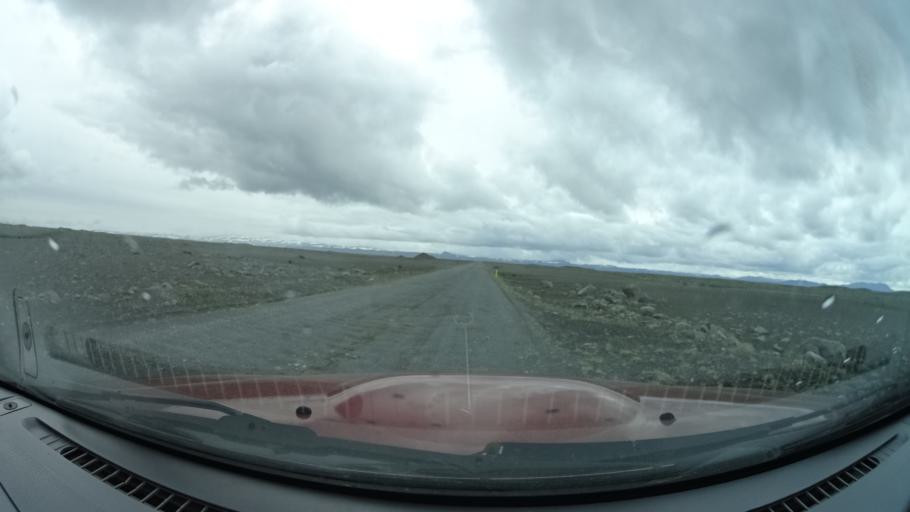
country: IS
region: Northeast
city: Laugar
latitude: 65.6974
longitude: -16.2946
